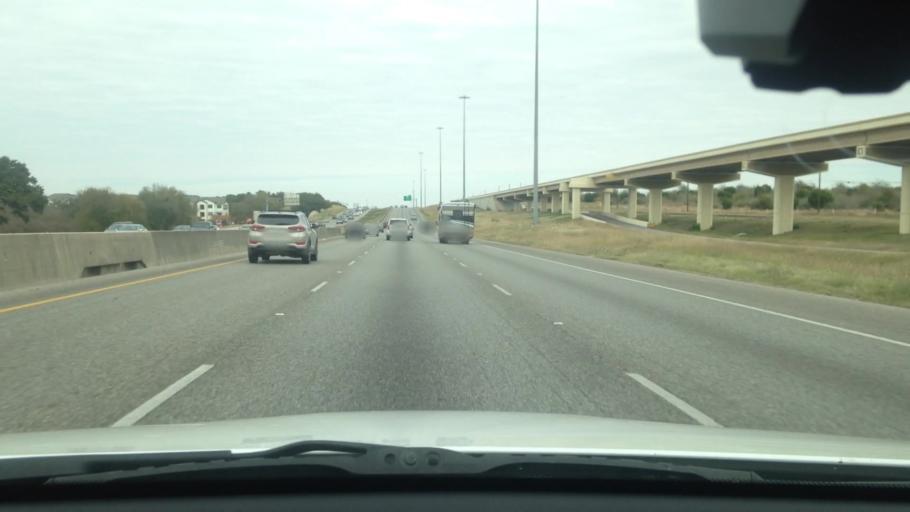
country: US
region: Texas
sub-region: Travis County
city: Onion Creek
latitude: 30.1158
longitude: -97.8057
